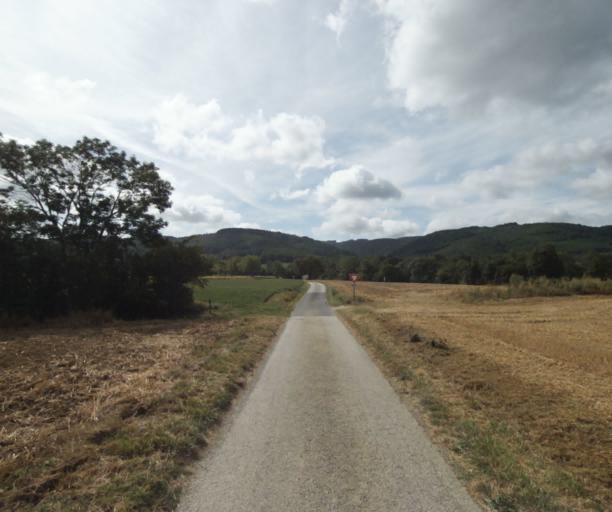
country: FR
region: Midi-Pyrenees
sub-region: Departement du Tarn
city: Soreze
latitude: 43.4715
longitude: 2.1008
